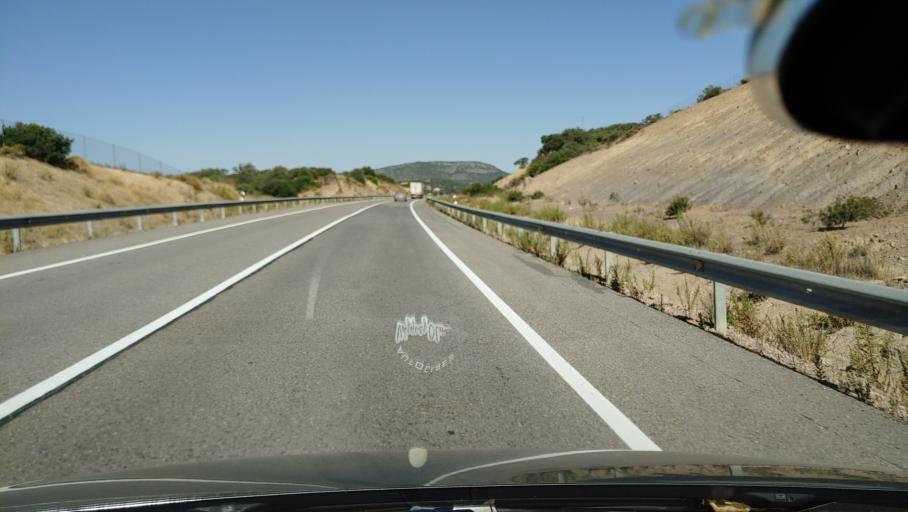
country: ES
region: Andalusia
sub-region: Province of Cordoba
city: Villaharta
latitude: 38.1381
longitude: -4.9561
